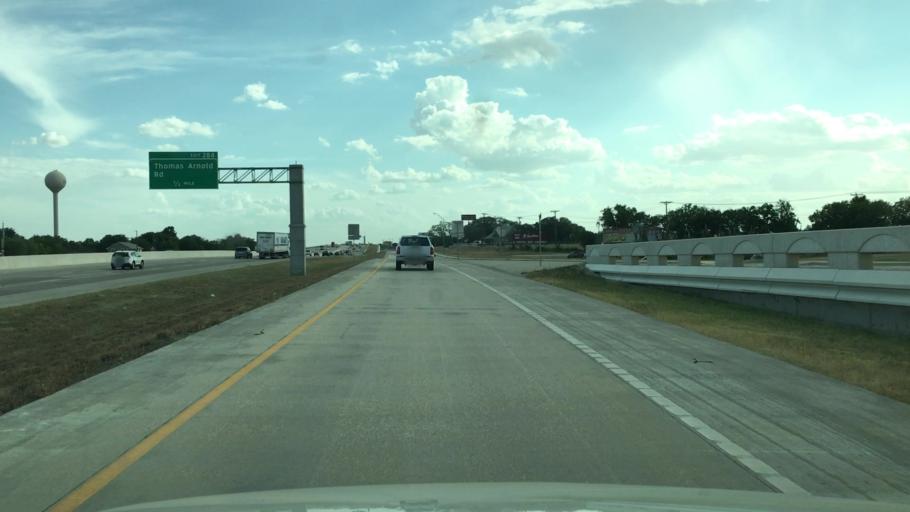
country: US
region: Texas
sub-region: Bell County
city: Salado
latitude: 30.9625
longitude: -97.5300
